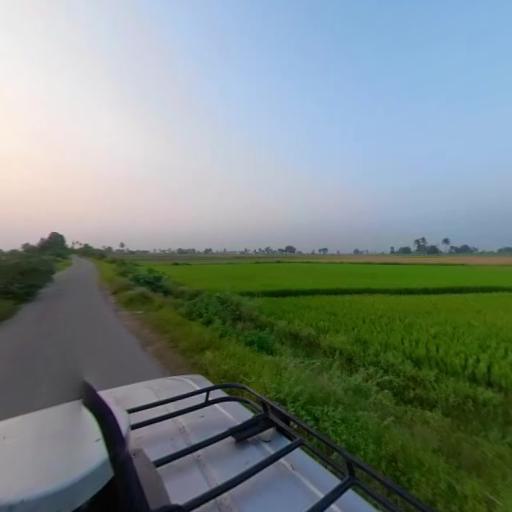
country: IN
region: Telangana
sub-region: Nalgonda
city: Suriapet
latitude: 17.0760
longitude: 79.5489
